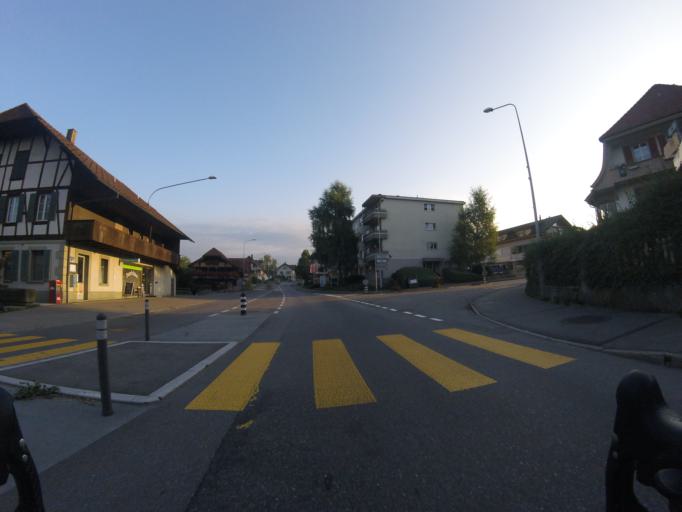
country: CH
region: Bern
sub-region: Bern-Mittelland District
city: Niederwichtrach
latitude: 46.8426
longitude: 7.5767
